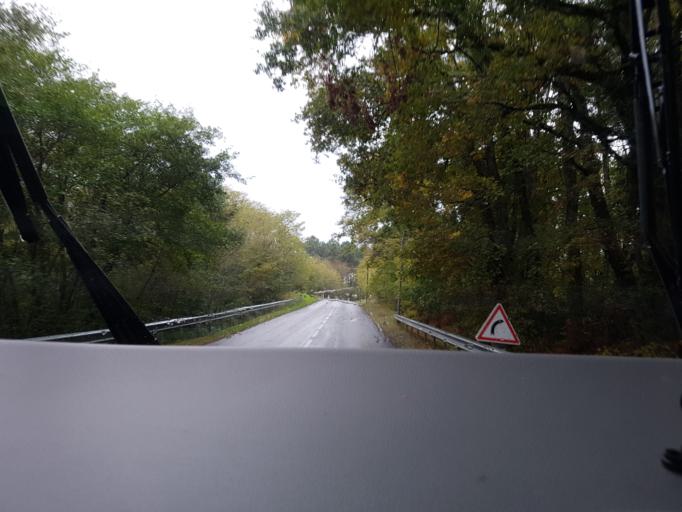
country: FR
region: Aquitaine
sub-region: Departement des Landes
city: Pissos
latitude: 44.3594
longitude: -0.6353
